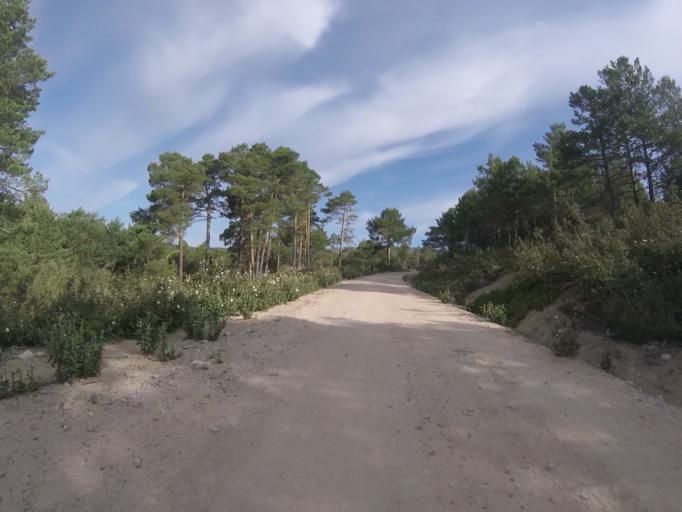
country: ES
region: Castille and Leon
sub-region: Provincia de Avila
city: Peguerinos
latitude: 40.6565
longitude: -4.1855
